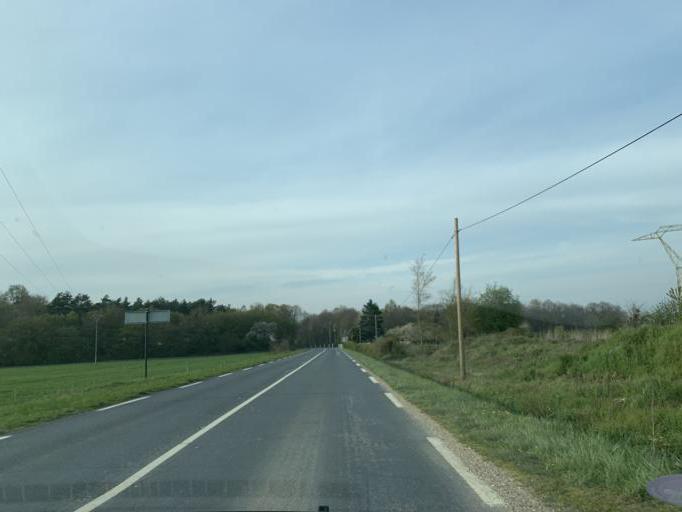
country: FR
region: Haute-Normandie
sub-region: Departement de la Seine-Maritime
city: Jumieges
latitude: 49.4152
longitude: 0.7965
